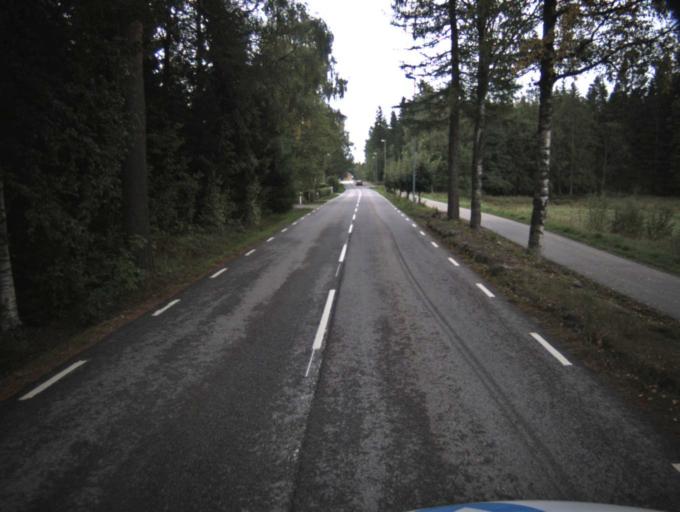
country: SE
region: Vaestra Goetaland
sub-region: Ulricehamns Kommun
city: Ulricehamn
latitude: 57.7765
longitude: 13.4284
